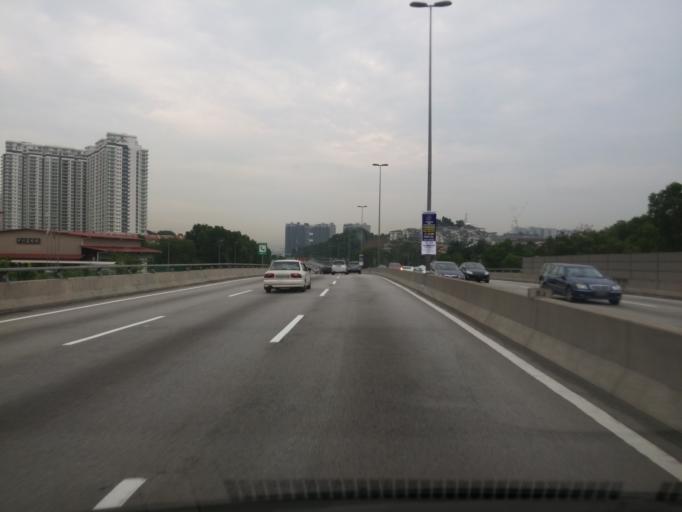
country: MY
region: Kuala Lumpur
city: Kuala Lumpur
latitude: 3.0741
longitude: 101.6888
